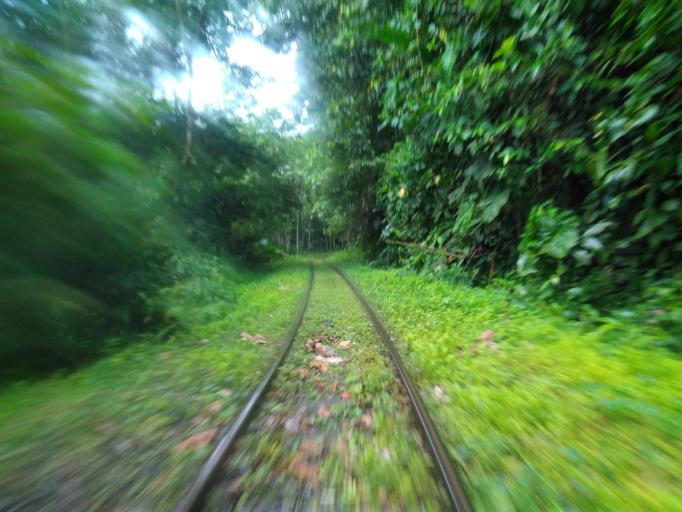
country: CO
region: Valle del Cauca
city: Buenaventura
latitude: 3.8456
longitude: -76.8828
